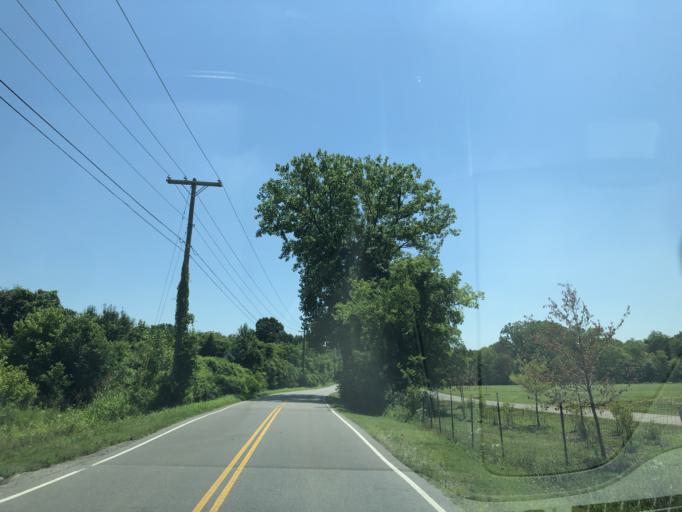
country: US
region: Tennessee
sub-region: Williamson County
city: Nolensville
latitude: 36.0285
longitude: -86.6697
